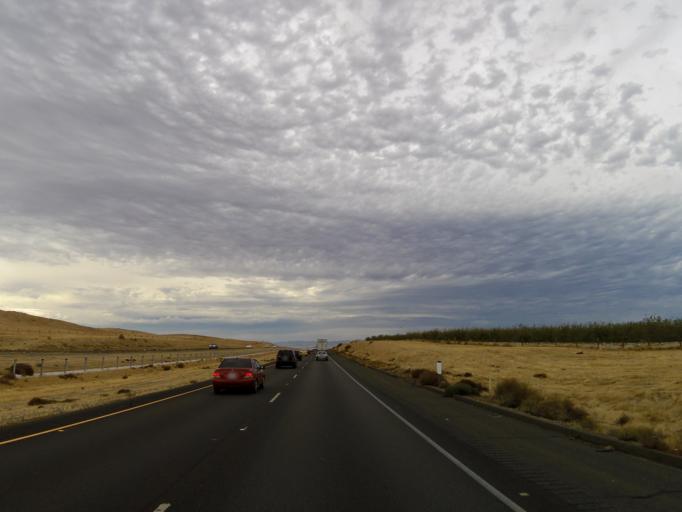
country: US
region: California
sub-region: Kings County
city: Avenal
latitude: 36.0556
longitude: -120.0665
